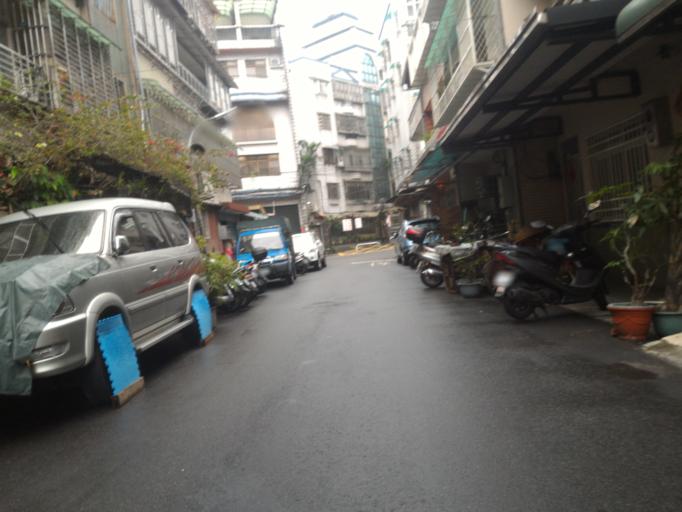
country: TW
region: Taipei
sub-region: Taipei
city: Banqiao
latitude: 25.0389
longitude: 121.4576
